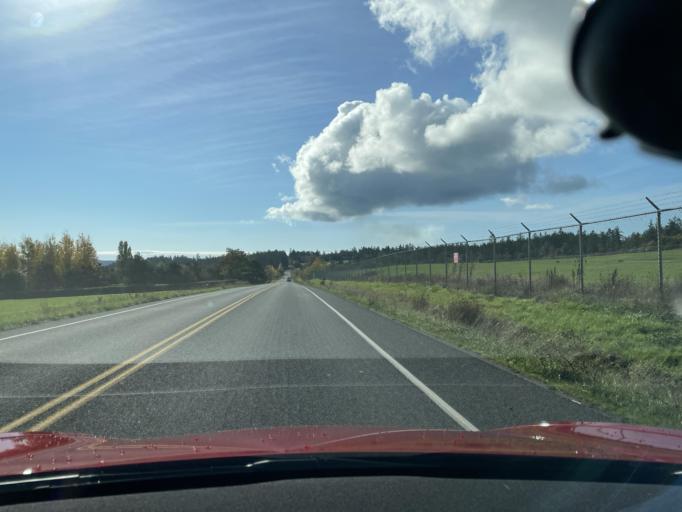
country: US
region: Washington
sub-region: San Juan County
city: Friday Harbor
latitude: 48.5192
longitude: -123.0231
